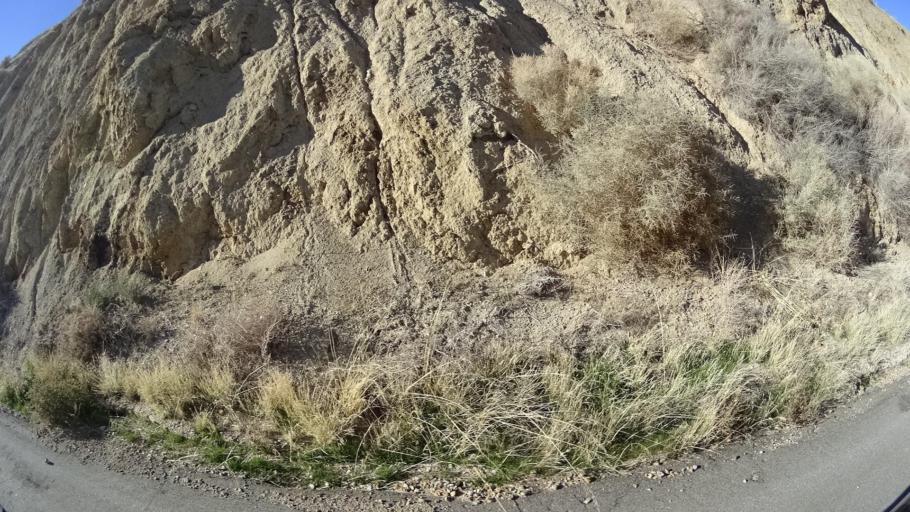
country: US
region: California
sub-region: Kern County
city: Maricopa
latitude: 34.9729
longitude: -119.4113
